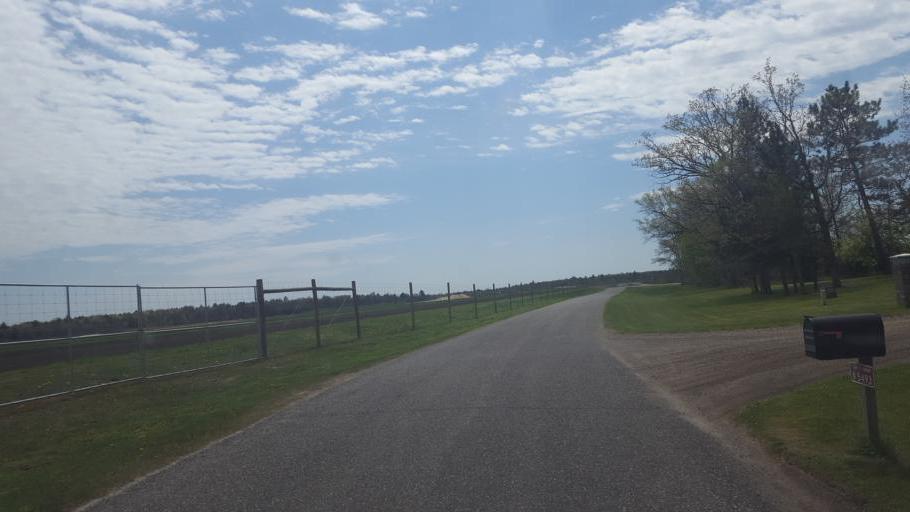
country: US
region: Wisconsin
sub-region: Monroe County
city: Tomah
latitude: 44.2655
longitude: -90.4853
